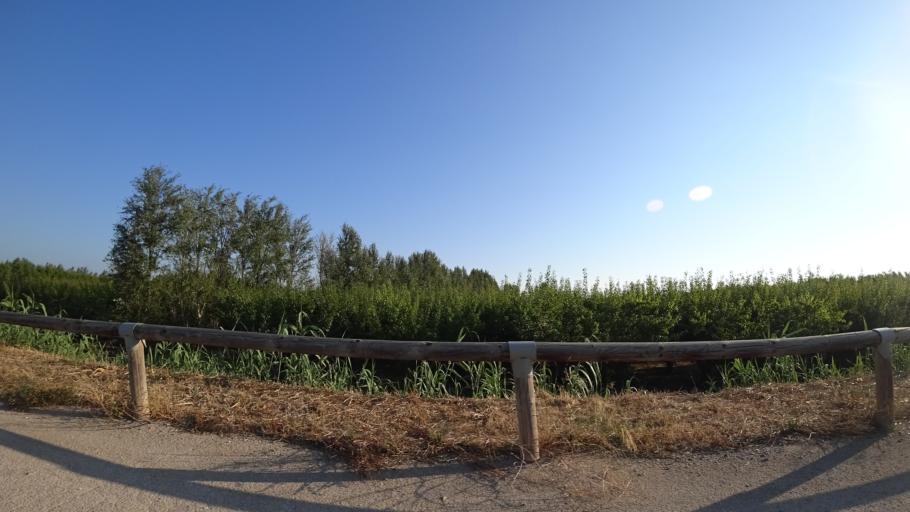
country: FR
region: Languedoc-Roussillon
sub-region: Departement des Pyrenees-Orientales
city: Pia
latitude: 42.7604
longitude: 2.9277
